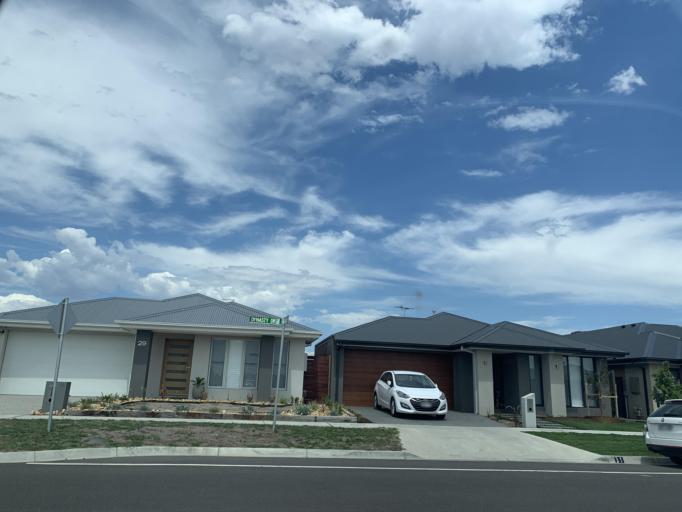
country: AU
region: Victoria
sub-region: Casey
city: Cranbourne South
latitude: -38.1255
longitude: 145.2403
